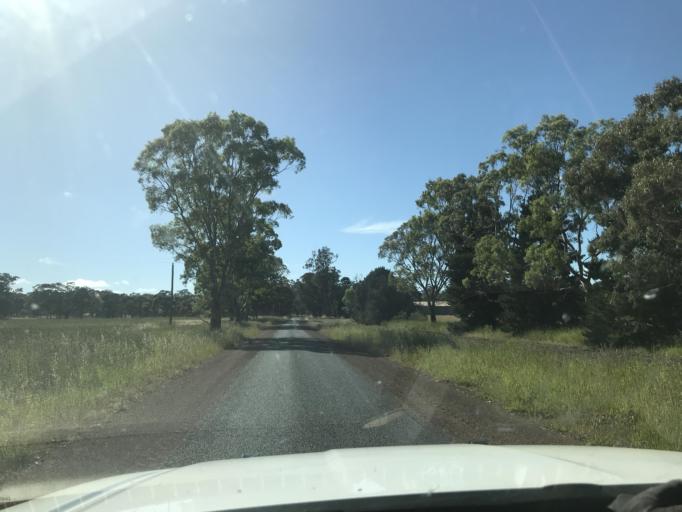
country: AU
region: Victoria
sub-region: Horsham
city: Horsham
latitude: -37.0915
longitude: 141.7695
